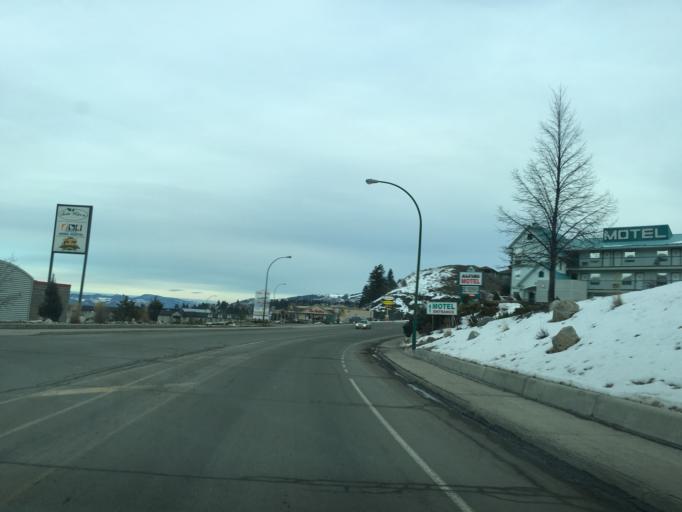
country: CA
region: British Columbia
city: Kamloops
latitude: 50.6516
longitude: -120.3775
